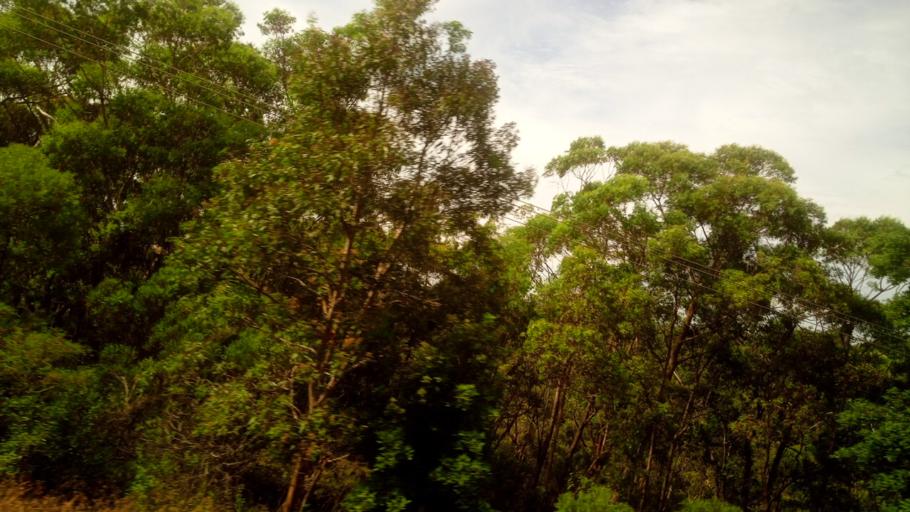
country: AU
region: New South Wales
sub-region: Blue Mountains Municipality
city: Hazelbrook
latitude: -33.7131
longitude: 150.5183
